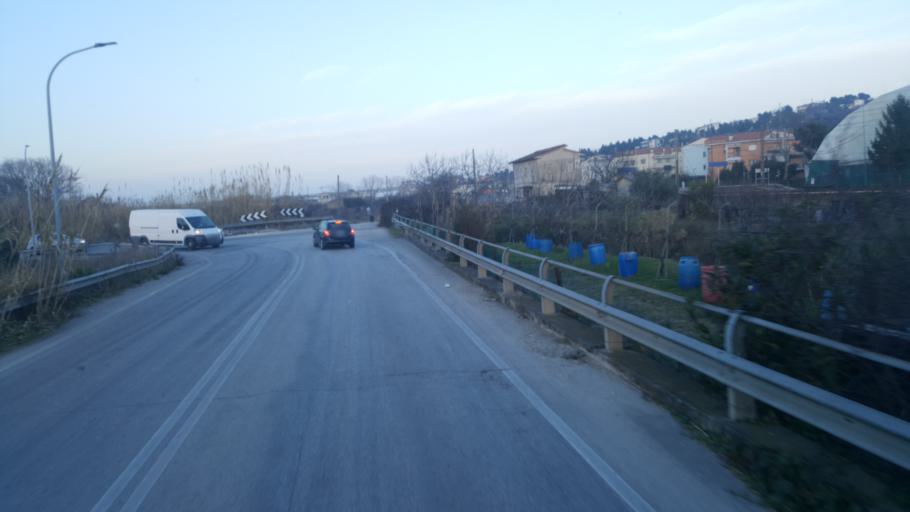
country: IT
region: The Marches
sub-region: Provincia di Ancona
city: Falconara Marittima
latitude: 43.6256
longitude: 13.3799
